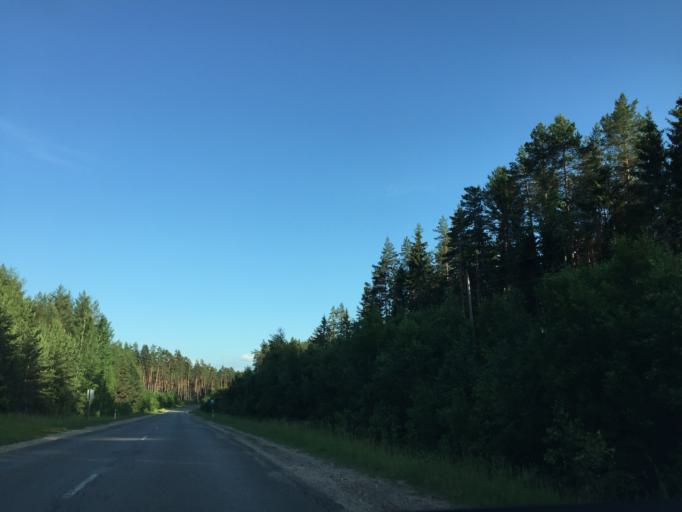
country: LV
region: Tukuma Rajons
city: Tukums
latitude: 57.0073
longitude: 23.1414
